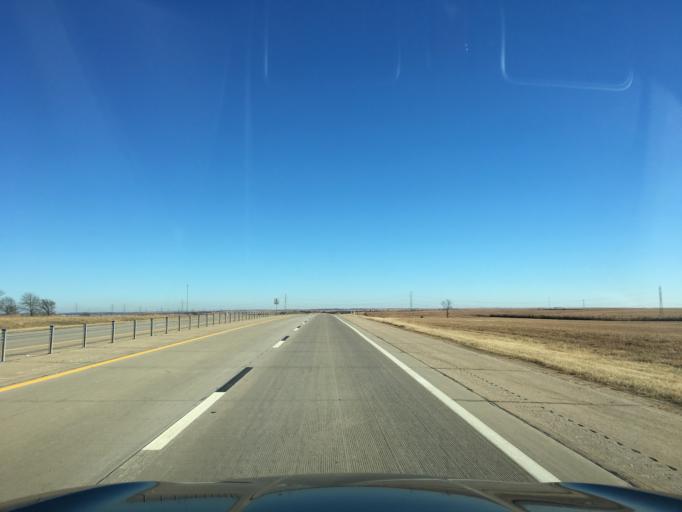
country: US
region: Oklahoma
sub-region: Noble County
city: Perry
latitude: 36.3921
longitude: -97.1200
